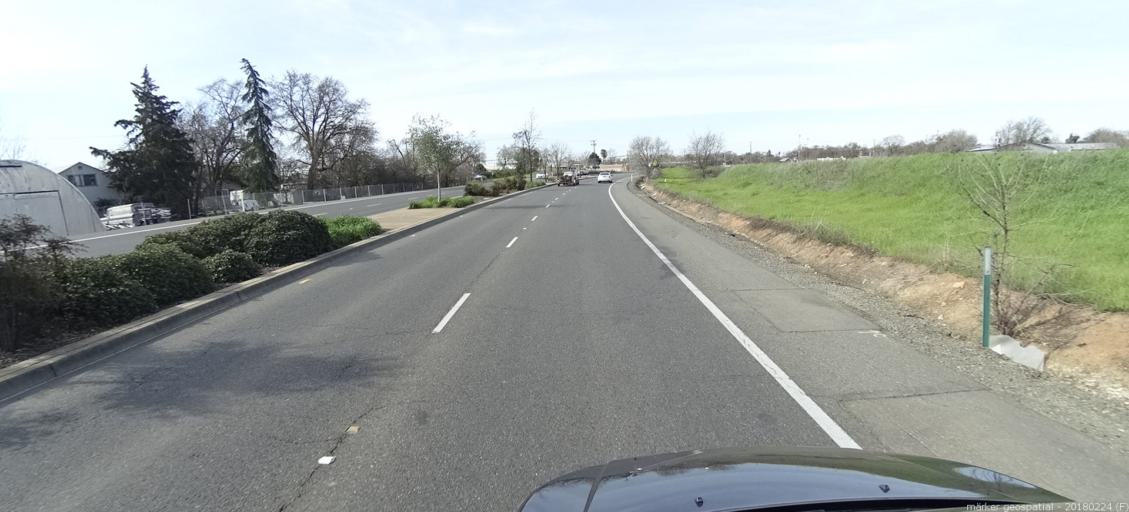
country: US
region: California
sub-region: Sacramento County
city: Rio Linda
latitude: 38.6846
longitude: -121.4352
